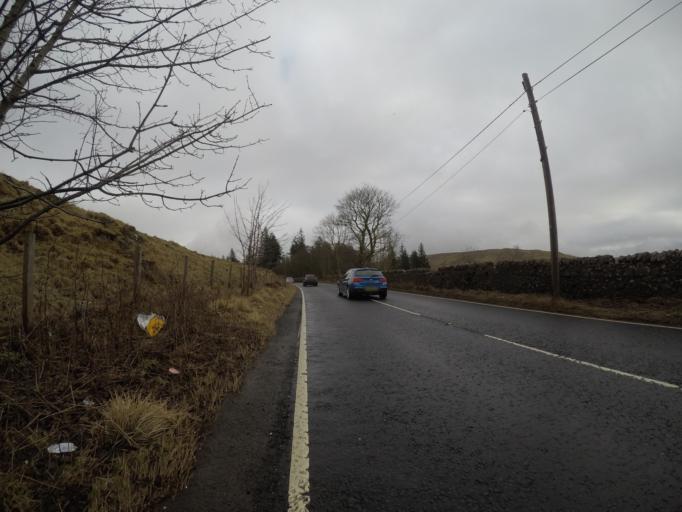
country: GB
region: Scotland
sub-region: North Ayrshire
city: Fairlie
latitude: 55.7753
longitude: -4.8367
